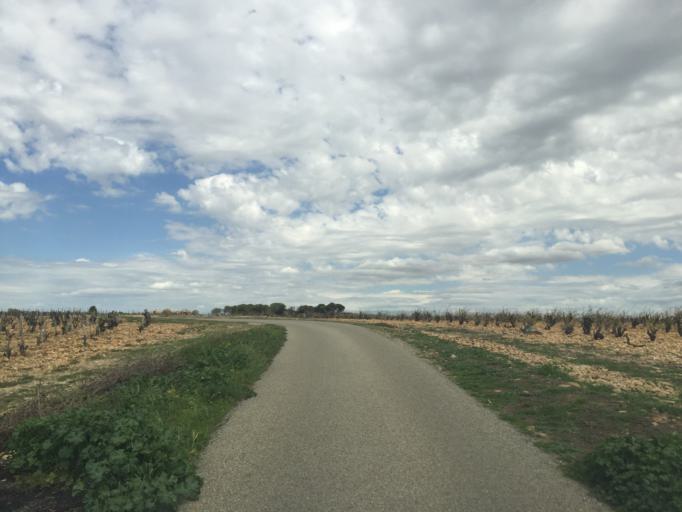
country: FR
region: Provence-Alpes-Cote d'Azur
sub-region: Departement du Vaucluse
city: Chateauneuf-du-Pape
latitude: 44.0526
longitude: 4.8557
